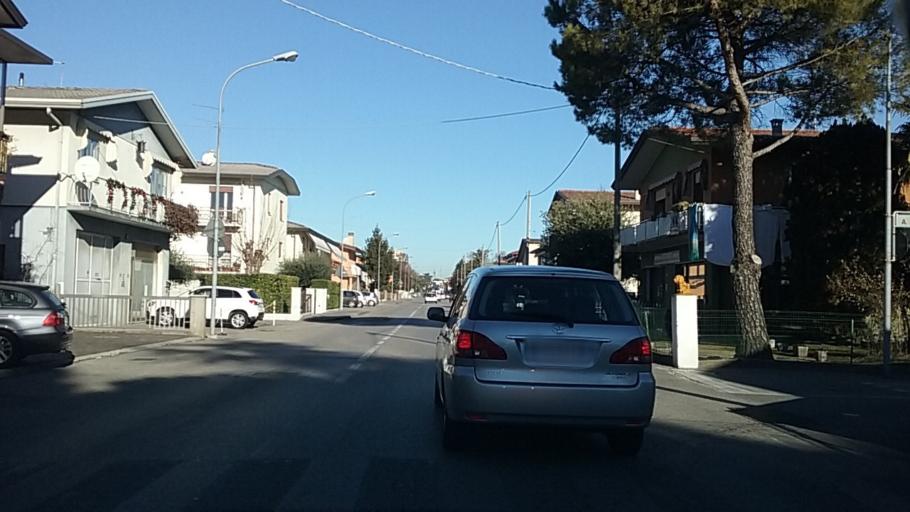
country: IT
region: Veneto
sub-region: Provincia di Venezia
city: San Dona di Piave
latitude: 45.6255
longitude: 12.5842
